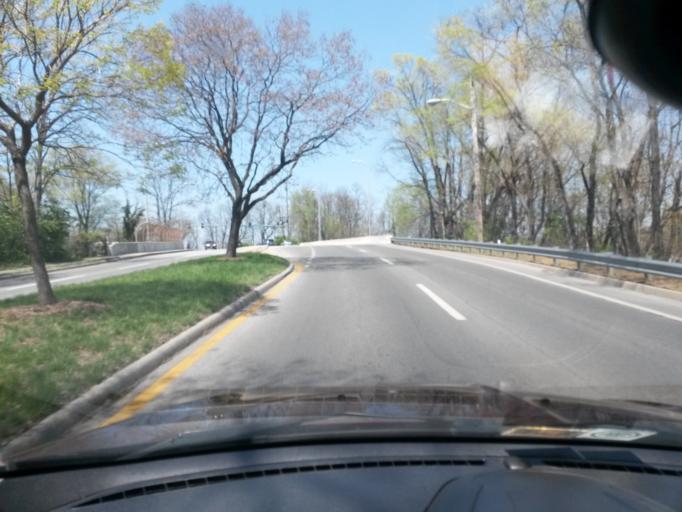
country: US
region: Virginia
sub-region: City of Roanoke
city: Roanoke
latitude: 37.2553
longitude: -79.9528
